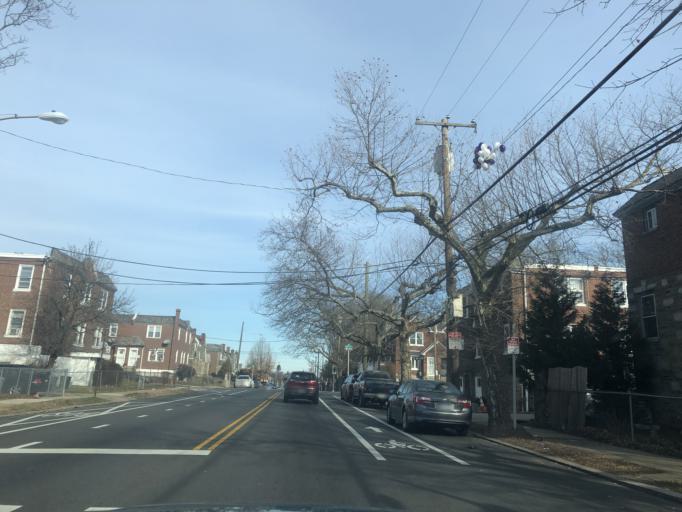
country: US
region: Pennsylvania
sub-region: Montgomery County
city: Wyncote
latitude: 40.0645
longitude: -75.1607
